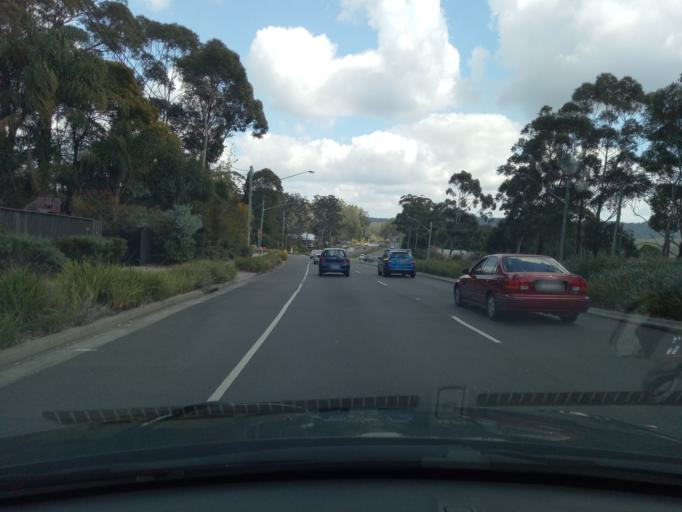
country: AU
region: New South Wales
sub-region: Gosford Shire
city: Erina
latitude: -33.4255
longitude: 151.4105
